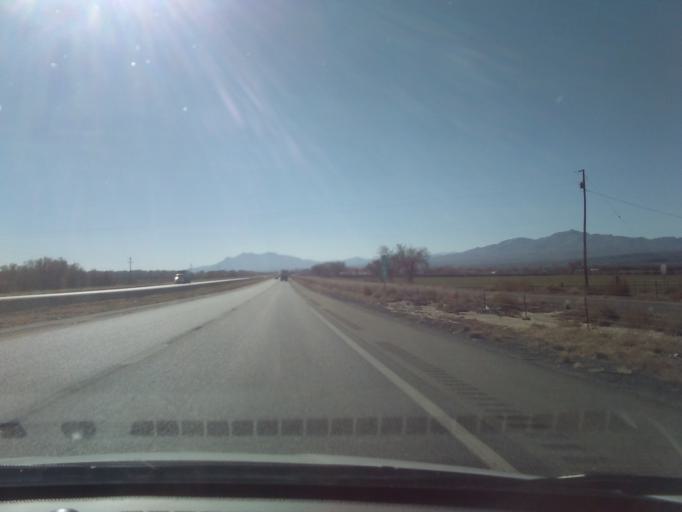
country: US
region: New Mexico
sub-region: Socorro County
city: Socorro
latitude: 34.2680
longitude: -106.9036
